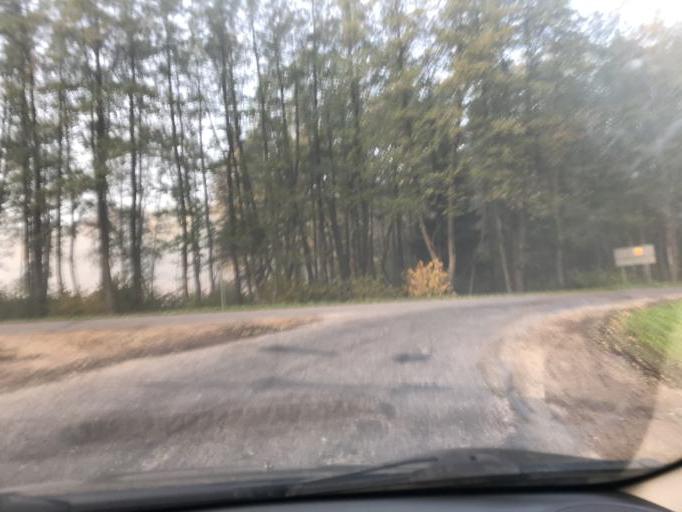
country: BY
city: Michanovichi
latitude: 53.7547
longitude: 27.6614
